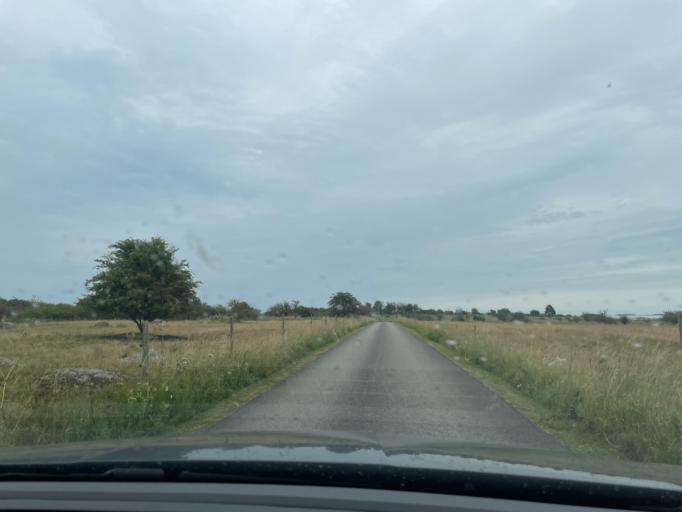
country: SE
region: Skane
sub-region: Bromolla Kommun
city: Bromoella
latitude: 56.0038
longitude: 14.4404
